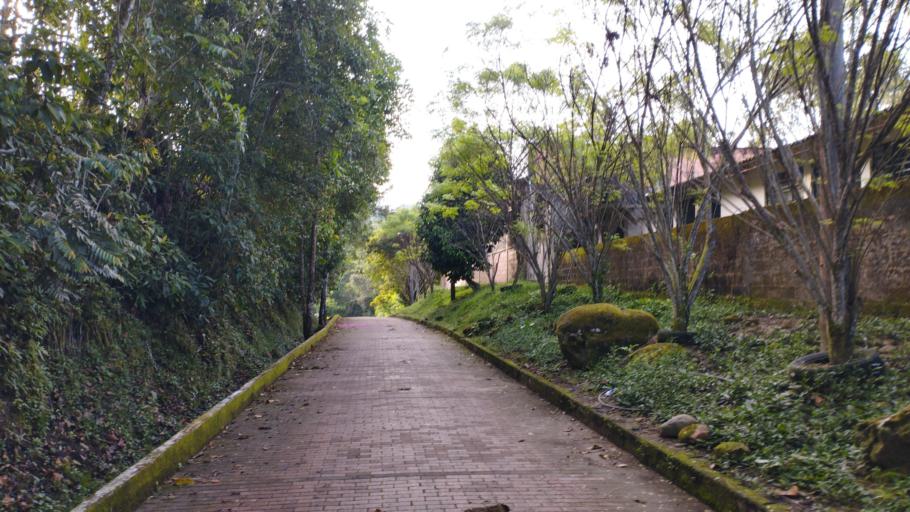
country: CO
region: Boyaca
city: San Luis de Gaceno
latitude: 4.8202
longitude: -73.1666
